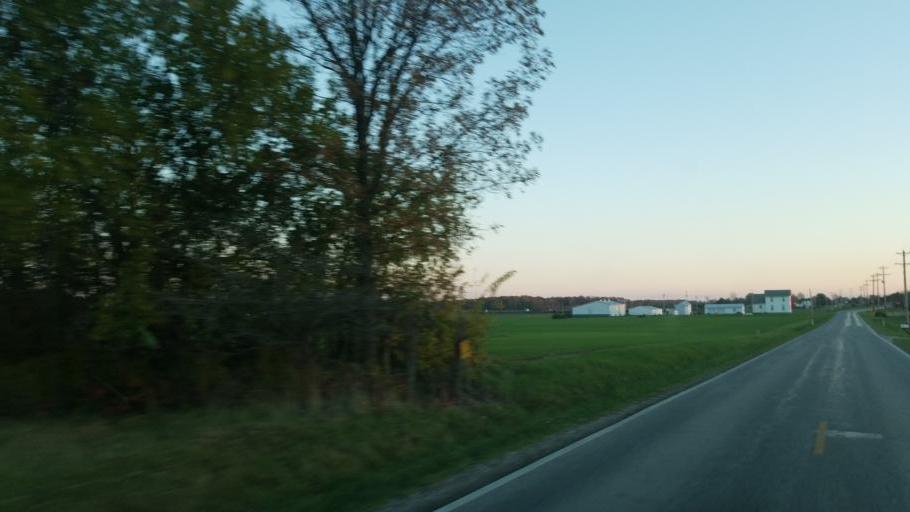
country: US
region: Ohio
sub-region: Huron County
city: Willard
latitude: 41.0755
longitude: -82.7831
